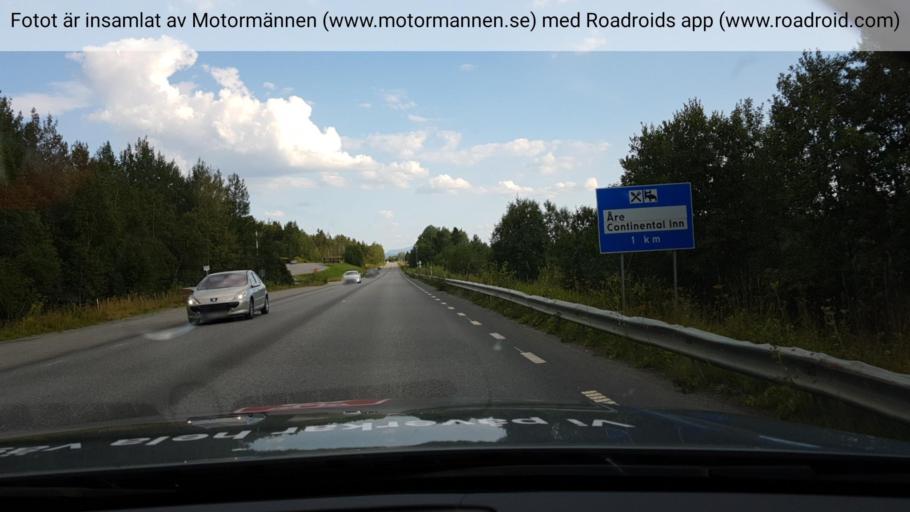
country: SE
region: Jaemtland
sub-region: Are Kommun
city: Are
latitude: 63.3752
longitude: 13.1593
